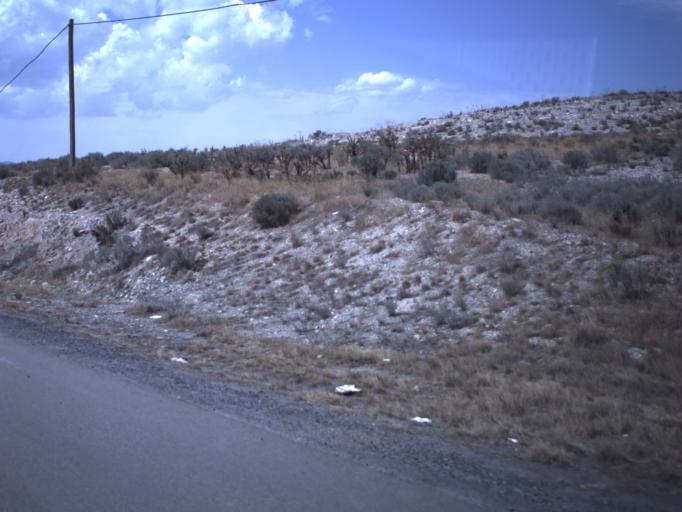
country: US
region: Utah
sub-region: Utah County
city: Saratoga Springs
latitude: 40.3831
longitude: -111.9601
